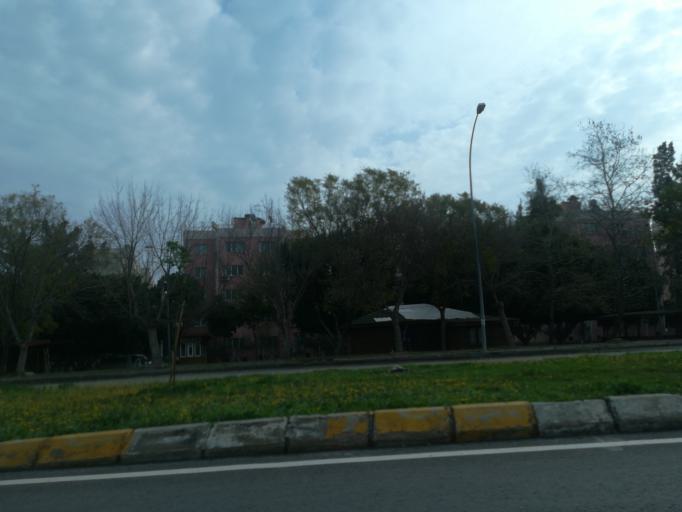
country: TR
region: Adana
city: Yuregir
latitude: 36.9912
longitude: 35.3625
